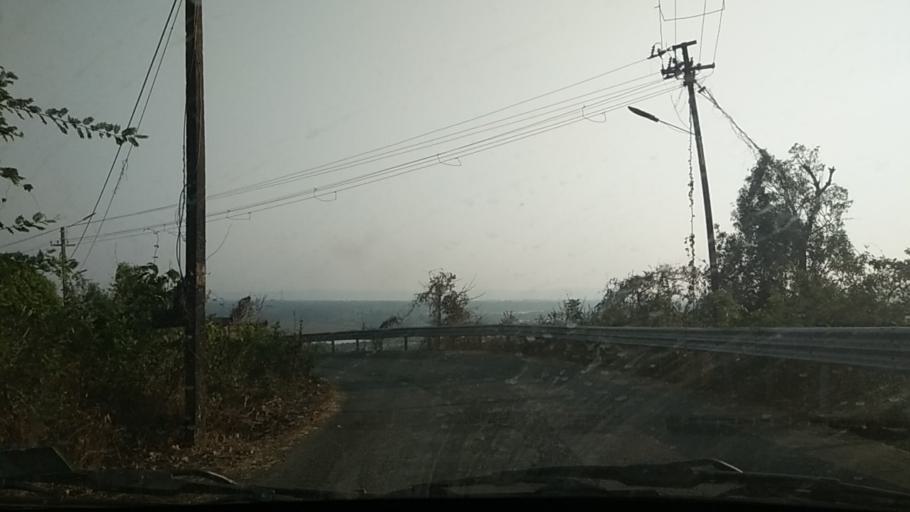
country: IN
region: Goa
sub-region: North Goa
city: Goa Velha
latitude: 15.4633
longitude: 73.8767
